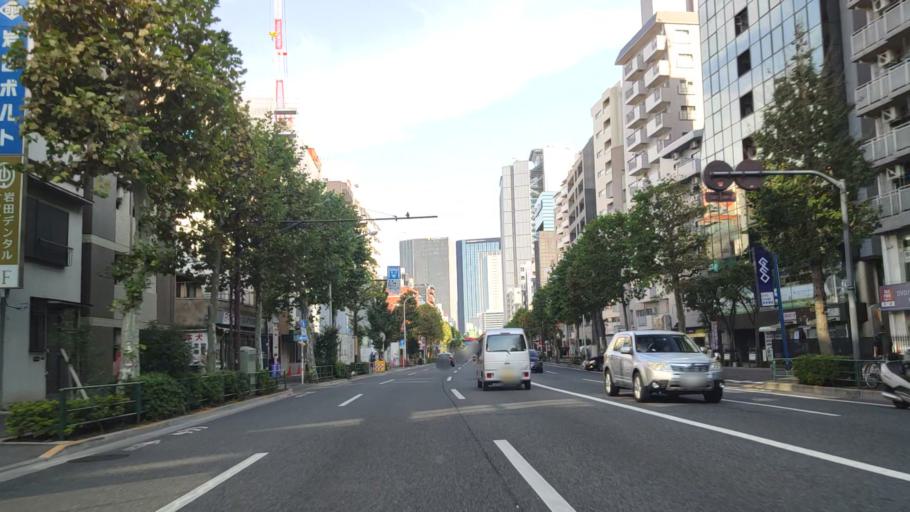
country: JP
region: Tokyo
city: Tokyo
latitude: 35.6976
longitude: 139.6767
